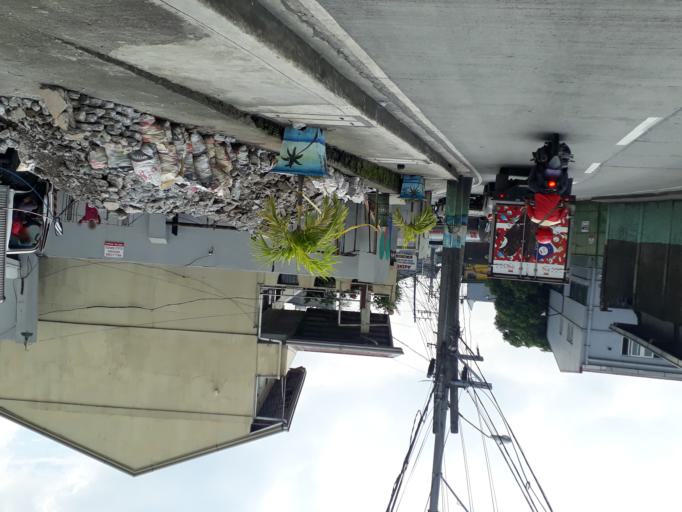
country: PH
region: Calabarzon
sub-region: Province of Rizal
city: Valenzuela
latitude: 14.7029
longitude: 120.9980
